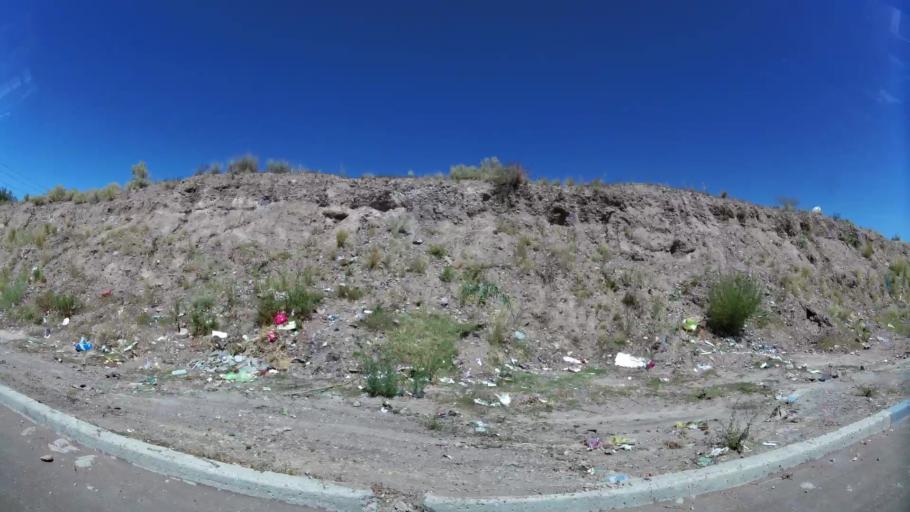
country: AR
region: Mendoza
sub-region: Departamento de Godoy Cruz
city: Godoy Cruz
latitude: -32.9472
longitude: -68.8756
